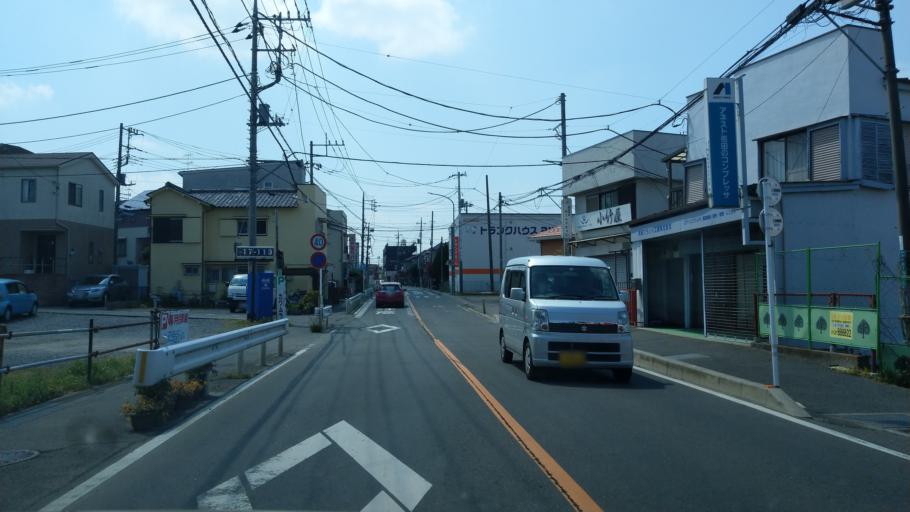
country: JP
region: Saitama
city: Saitama
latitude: 35.8897
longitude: 139.6637
